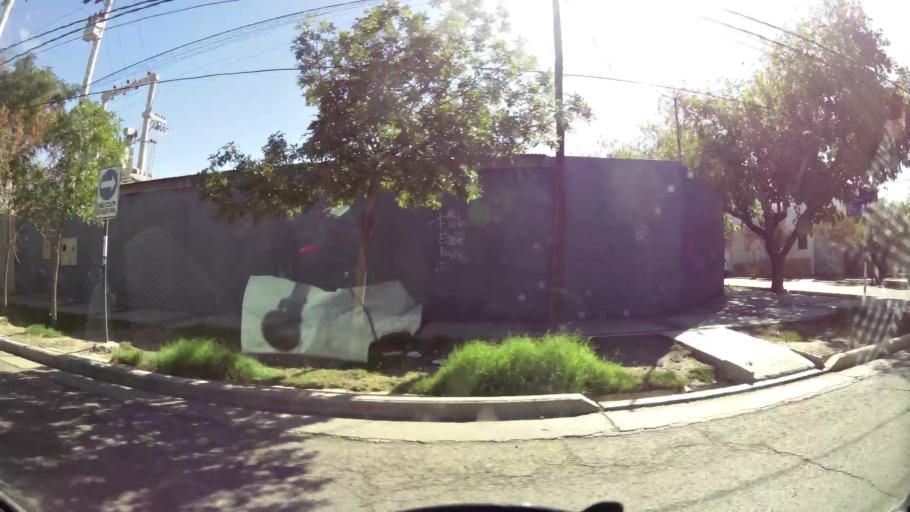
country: AR
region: San Juan
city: San Juan
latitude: -31.5284
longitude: -68.5360
